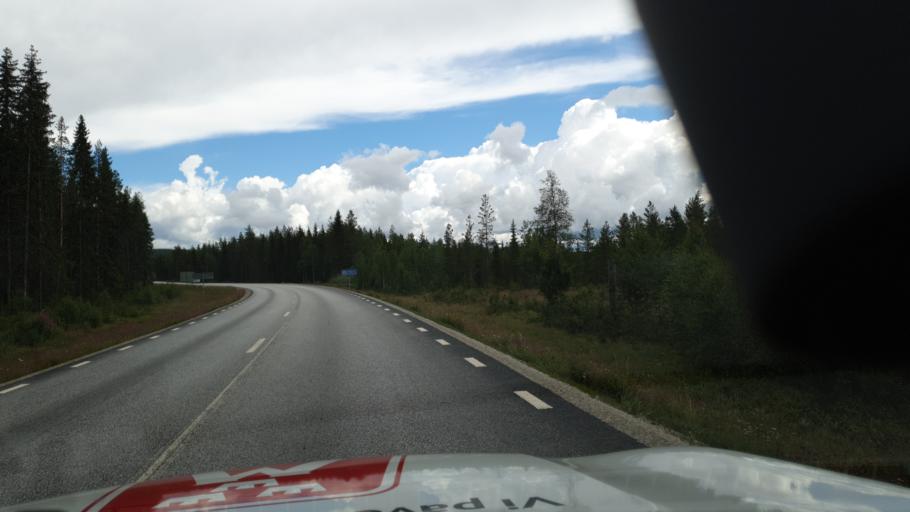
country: SE
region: Vaesterbotten
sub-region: Vindelns Kommun
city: Vindeln
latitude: 64.0559
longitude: 19.6509
